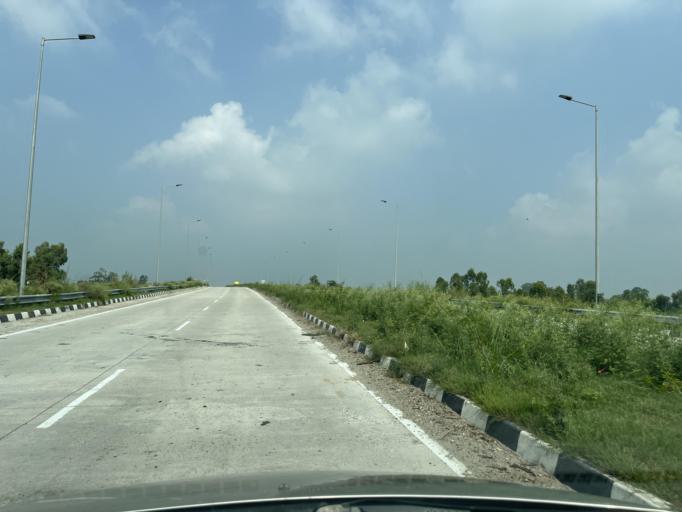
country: IN
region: Uttarakhand
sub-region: Udham Singh Nagar
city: Kashipur
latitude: 29.1714
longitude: 78.9506
